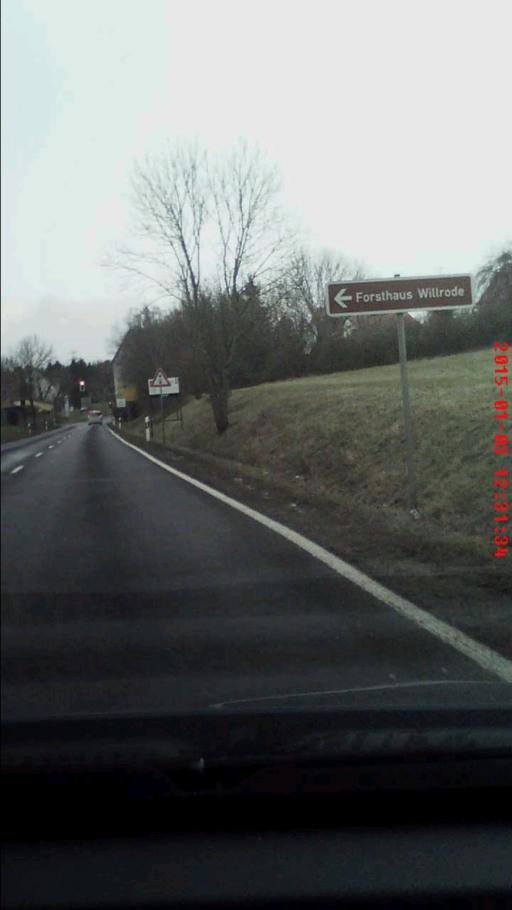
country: DE
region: Thuringia
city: Klettbach
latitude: 50.9144
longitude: 11.1550
